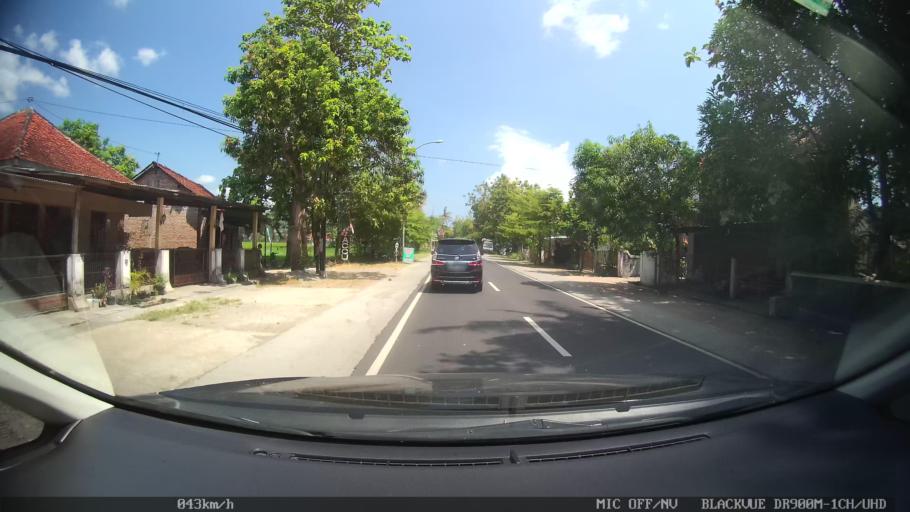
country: ID
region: Daerah Istimewa Yogyakarta
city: Pundong
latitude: -7.9235
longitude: 110.3743
